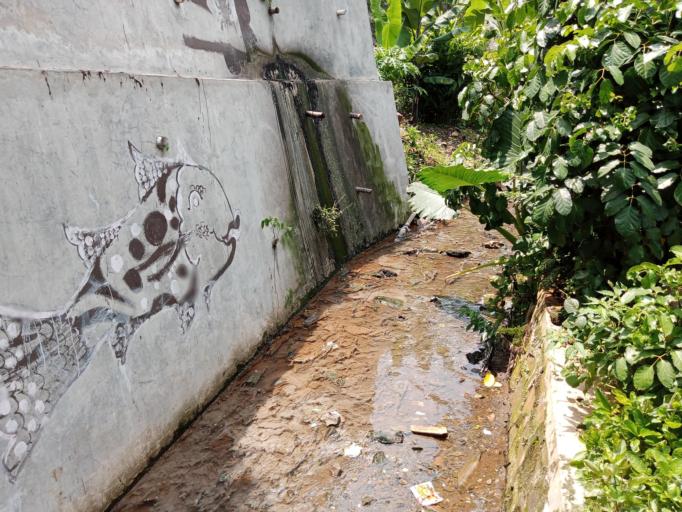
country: ID
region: West Java
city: Depok
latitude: -6.4044
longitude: 106.8102
